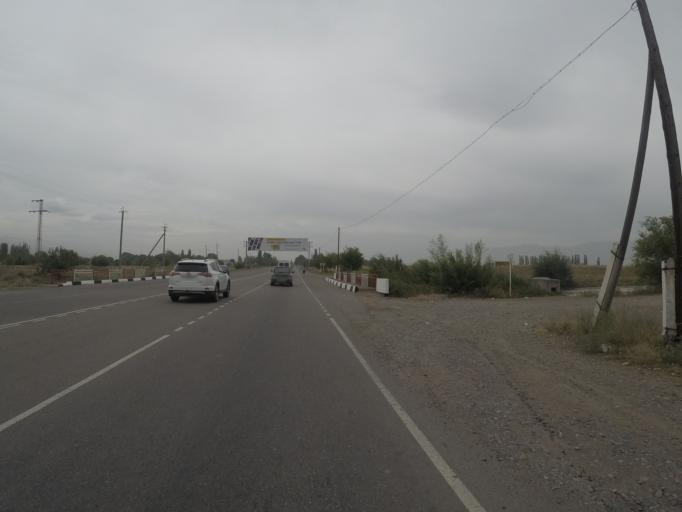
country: KG
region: Chuy
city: Bystrovka
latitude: 42.8238
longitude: 75.5500
